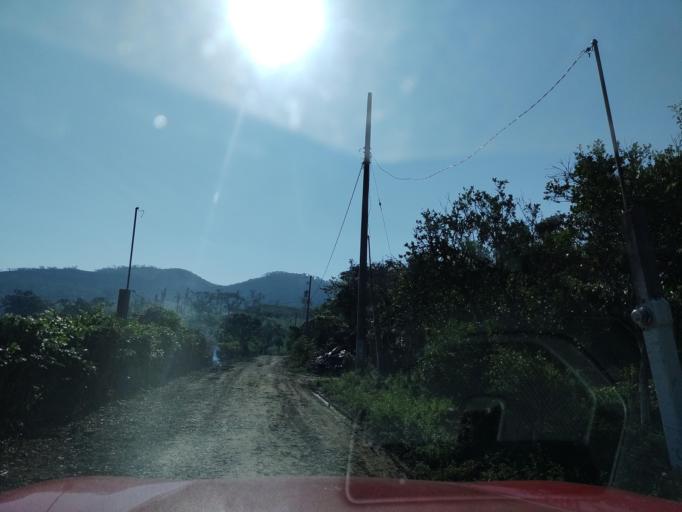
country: MX
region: Veracruz
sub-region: Papantla
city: Polutla
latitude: 20.5154
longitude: -97.2435
